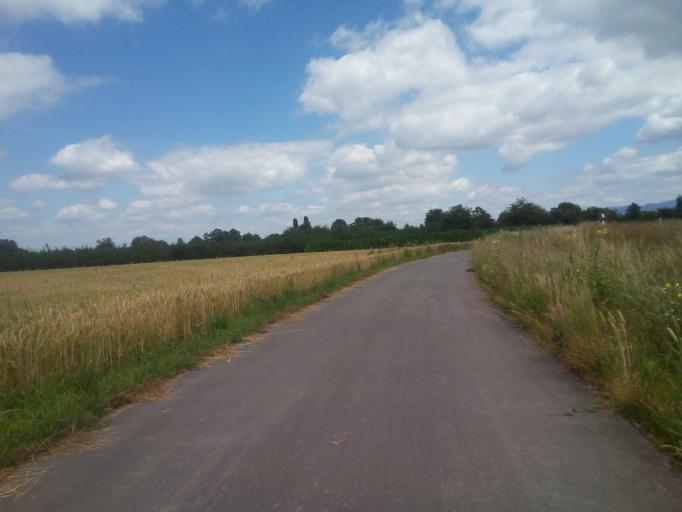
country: DE
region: Baden-Wuerttemberg
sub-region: Freiburg Region
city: Renchen
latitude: 48.6160
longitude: 7.9823
